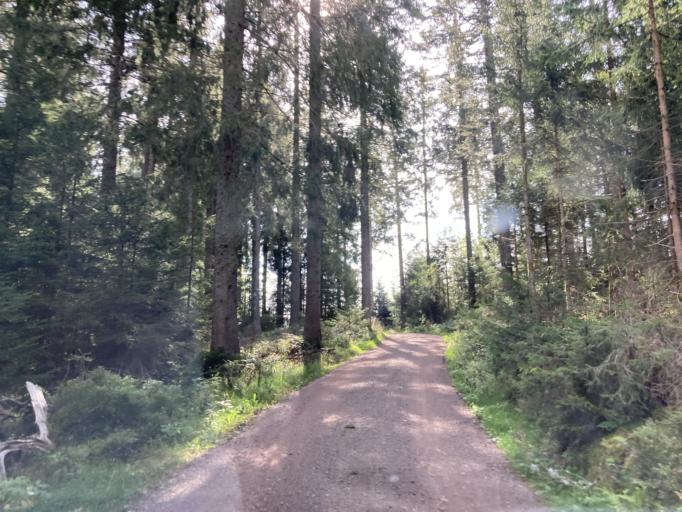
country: DE
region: Baden-Wuerttemberg
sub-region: Freiburg Region
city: Schonwald im Schwarzwald
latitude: 48.0809
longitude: 8.2188
